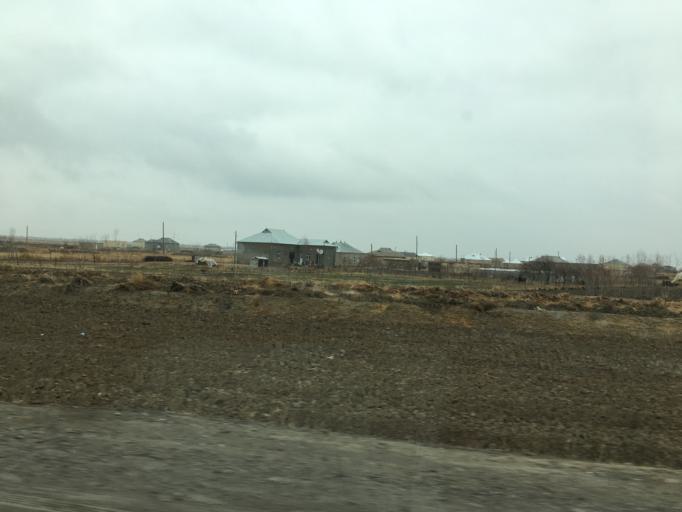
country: TM
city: Murgab
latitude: 37.4717
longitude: 62.0258
